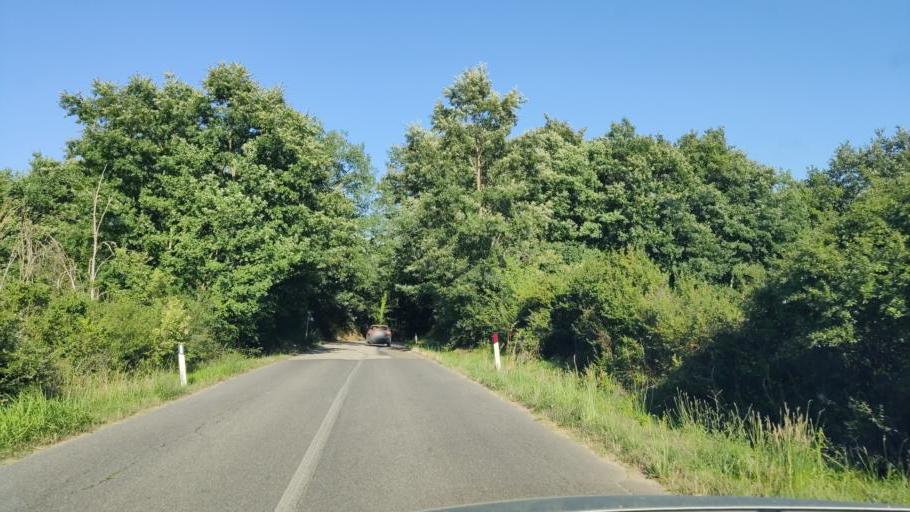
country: IT
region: Umbria
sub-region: Provincia di Terni
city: Penna in Teverina
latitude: 42.4832
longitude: 12.3701
